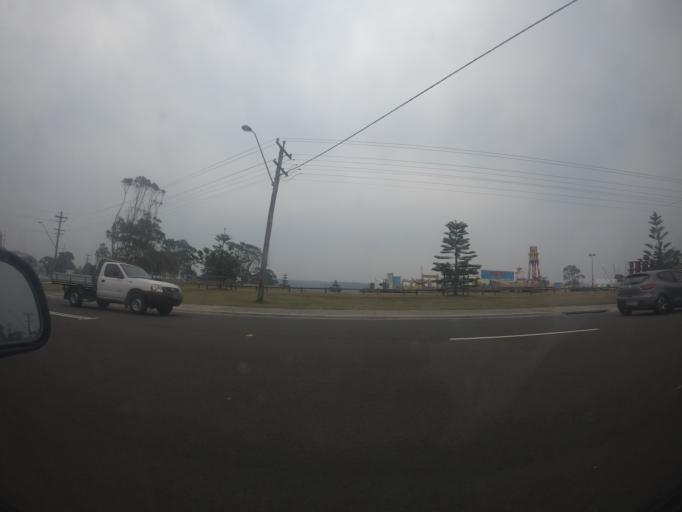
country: AU
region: New South Wales
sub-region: Shellharbour
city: Shellharbour Village
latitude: -34.5809
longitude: 150.8629
